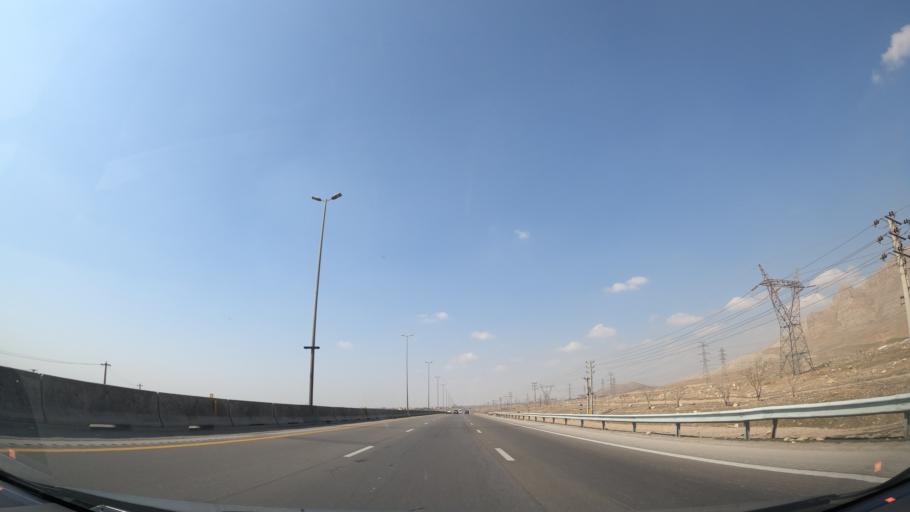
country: IR
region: Qazvin
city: Abyek
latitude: 36.0540
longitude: 50.5113
